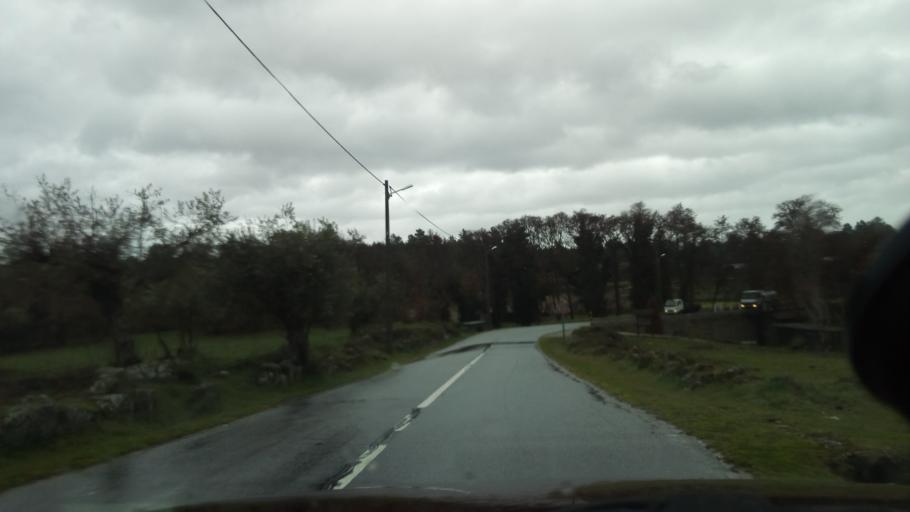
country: PT
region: Guarda
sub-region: Fornos de Algodres
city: Fornos de Algodres
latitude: 40.5865
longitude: -7.5115
